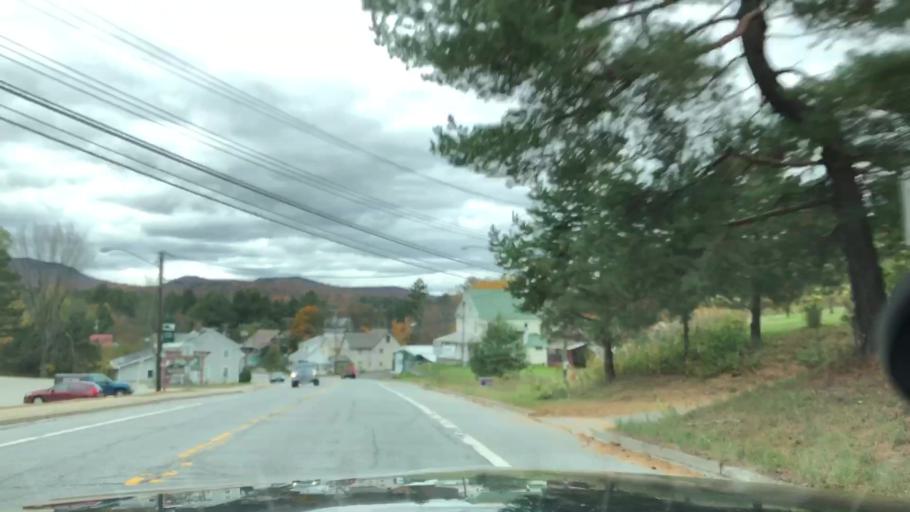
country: US
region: New York
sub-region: Franklin County
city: Tupper Lake
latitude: 43.9685
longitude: -74.4152
